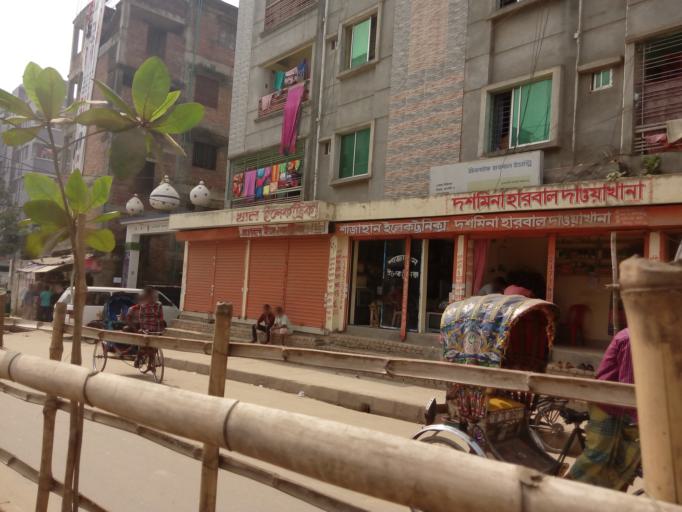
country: BD
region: Dhaka
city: Tungi
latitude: 23.8138
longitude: 90.3734
